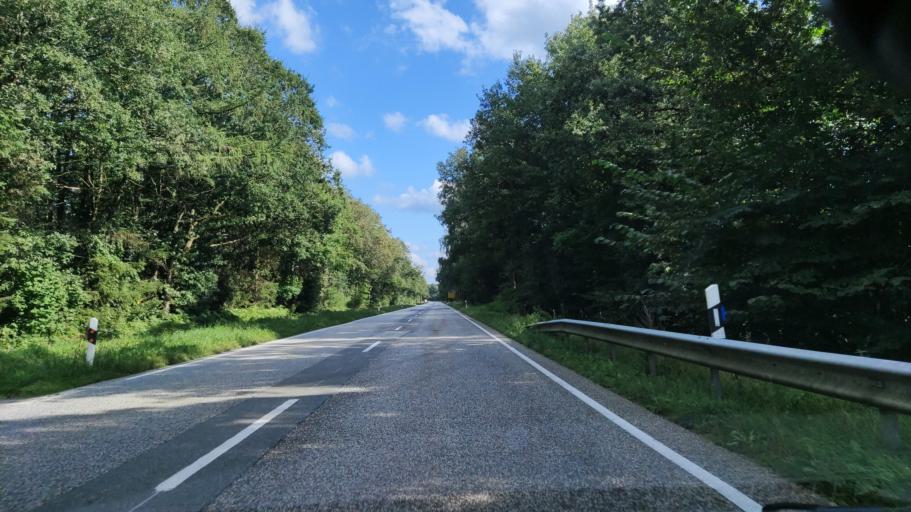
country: DE
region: Schleswig-Holstein
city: Jevenstedt
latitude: 54.2193
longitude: 9.7165
